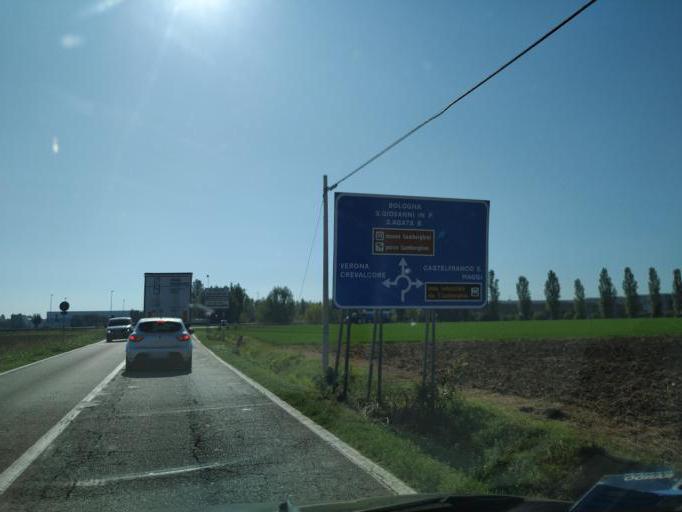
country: IT
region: Emilia-Romagna
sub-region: Provincia di Bologna
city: Sant'Agata Bolognese
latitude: 44.6631
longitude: 11.1151
